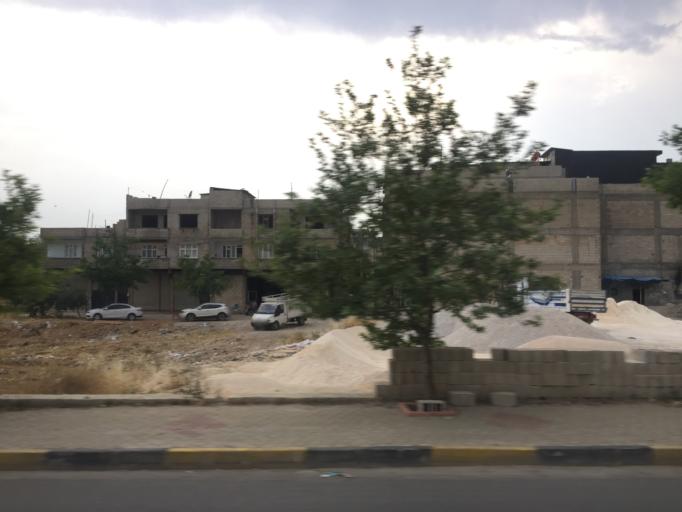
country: TR
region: Gaziantep
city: Gaziantep
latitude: 37.0626
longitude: 37.4155
